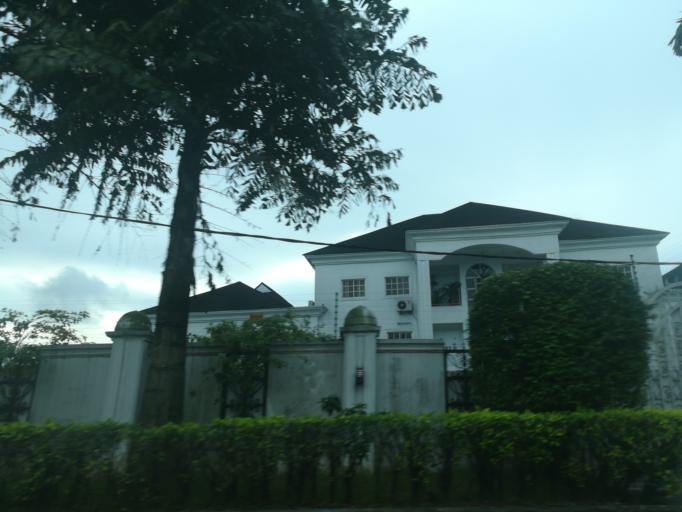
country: NG
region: Rivers
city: Port Harcourt
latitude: 4.8209
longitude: 6.9923
